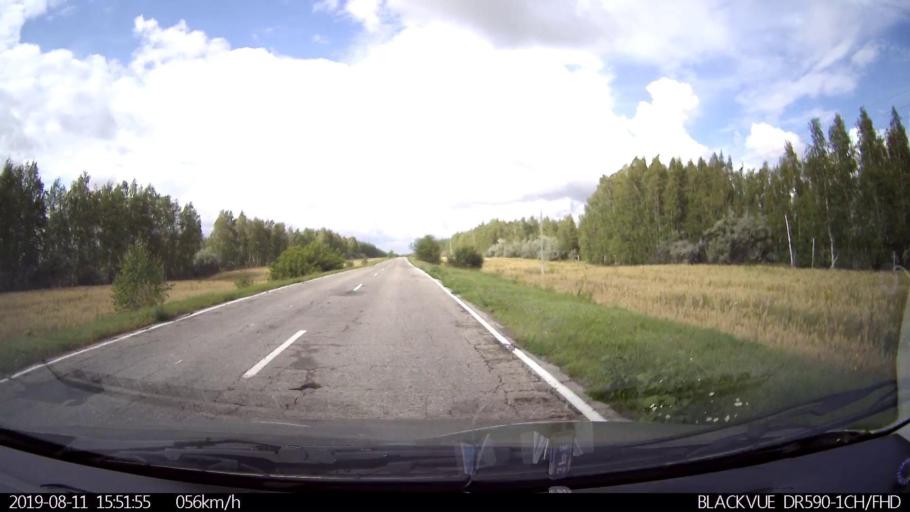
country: RU
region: Ulyanovsk
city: Ignatovka
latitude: 53.9225
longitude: 47.6562
